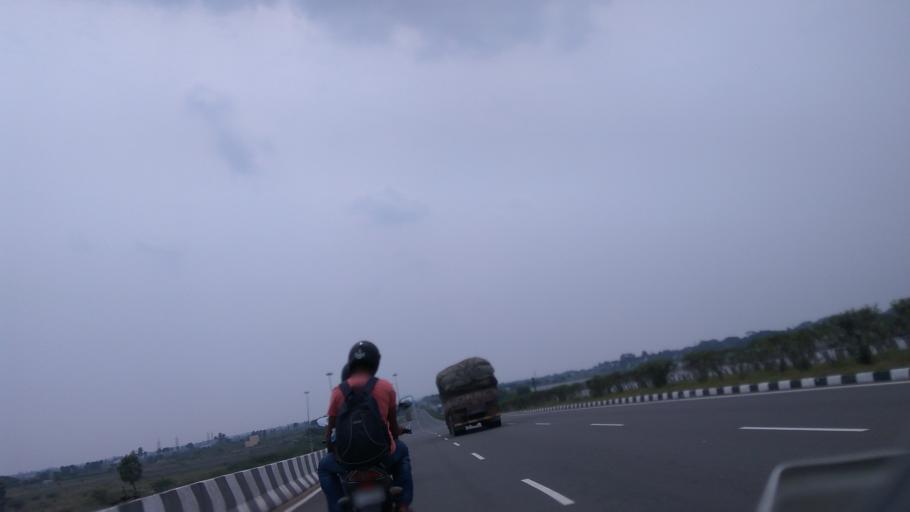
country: IN
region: Tamil Nadu
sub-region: Dharmapuri
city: Dharmapuri
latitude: 12.1393
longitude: 78.1395
